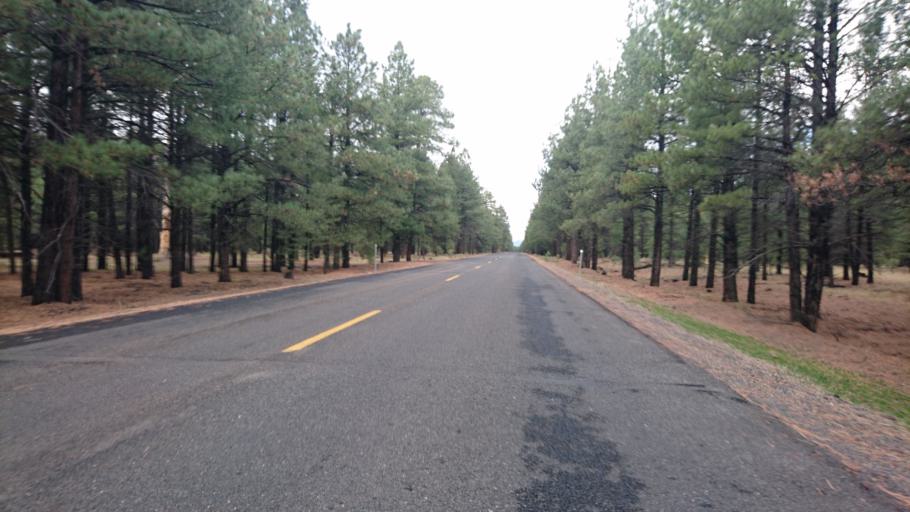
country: US
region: Arizona
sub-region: Coconino County
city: Parks
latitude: 35.2560
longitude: -111.8649
